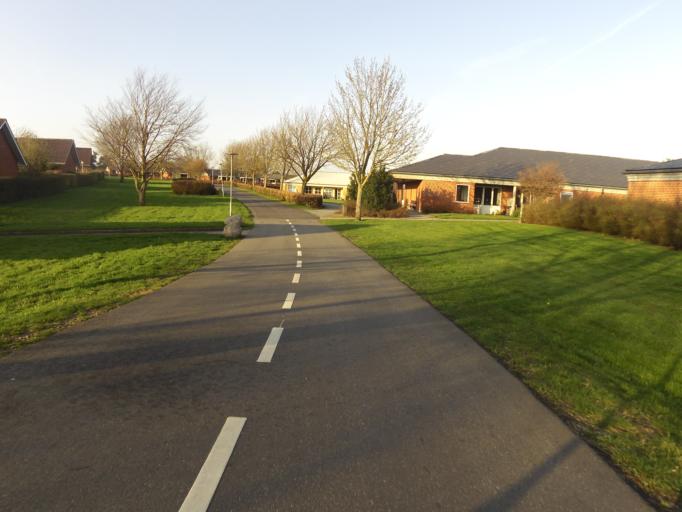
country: DK
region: South Denmark
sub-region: Vejen Kommune
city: Vejen
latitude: 55.4792
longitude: 9.1286
